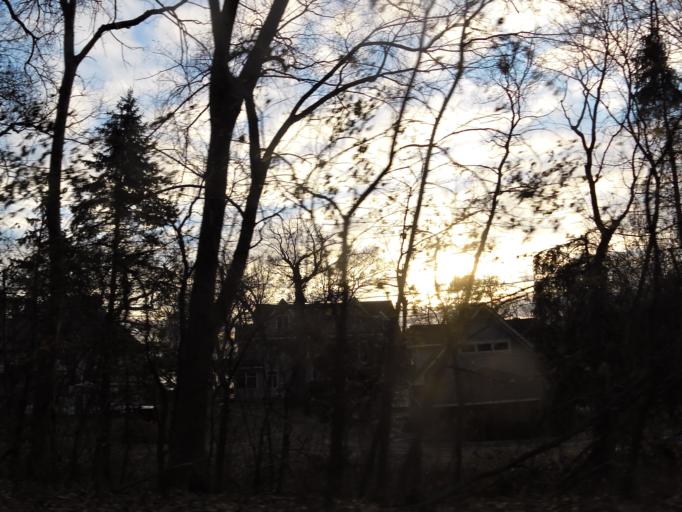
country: US
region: Minnesota
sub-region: Washington County
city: Dellwood
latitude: 45.0945
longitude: -92.9810
